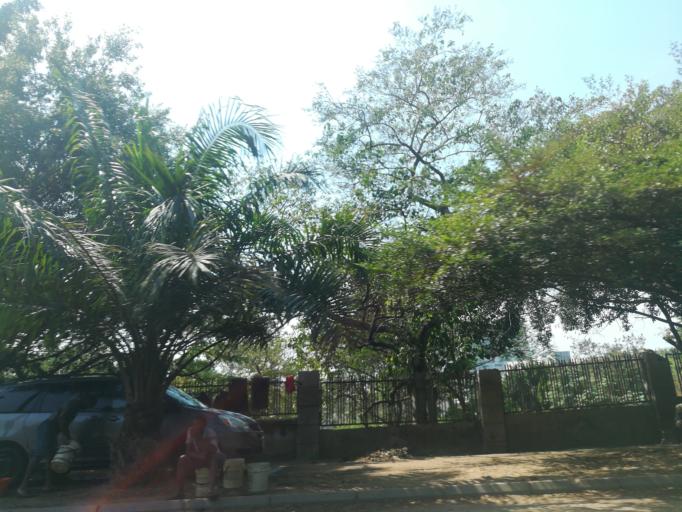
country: NG
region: Abuja Federal Capital Territory
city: Abuja
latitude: 9.0700
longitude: 7.4370
